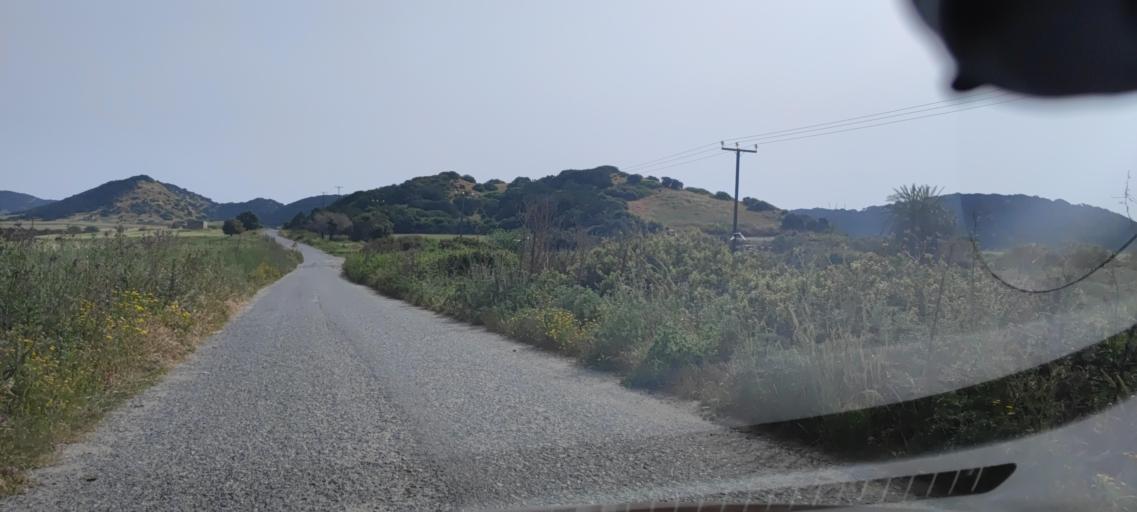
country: CY
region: Ammochostos
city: Rizokarpaso
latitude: 35.6296
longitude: 34.4941
